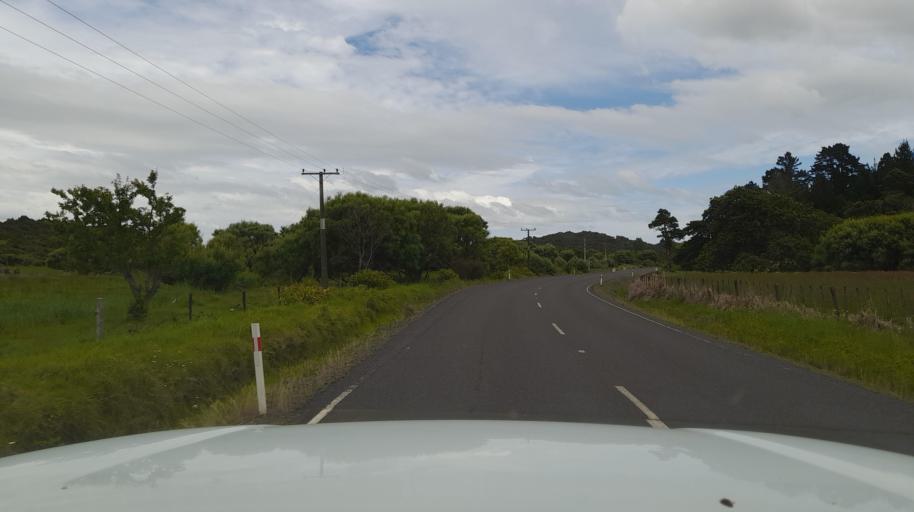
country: NZ
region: Northland
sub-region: Far North District
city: Kaitaia
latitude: -35.3857
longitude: 173.3841
